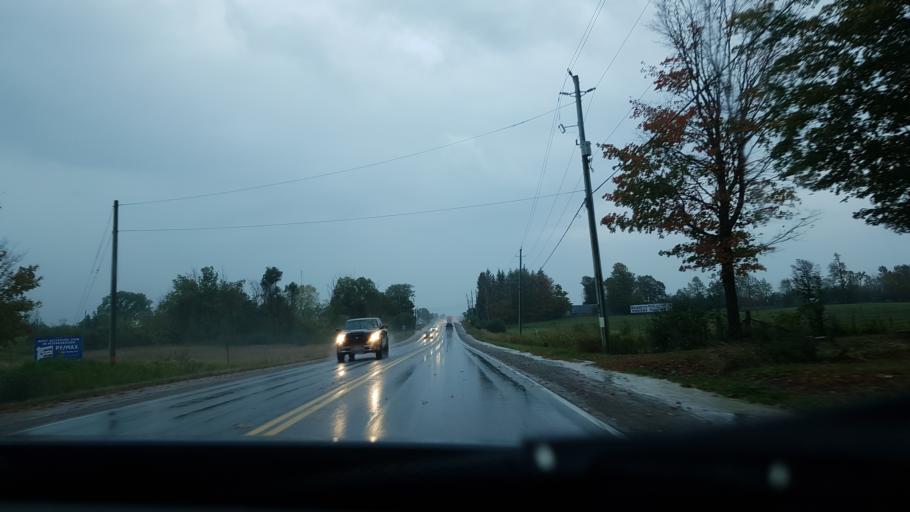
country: CA
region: Ontario
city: Peterborough
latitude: 44.3543
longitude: -78.3671
